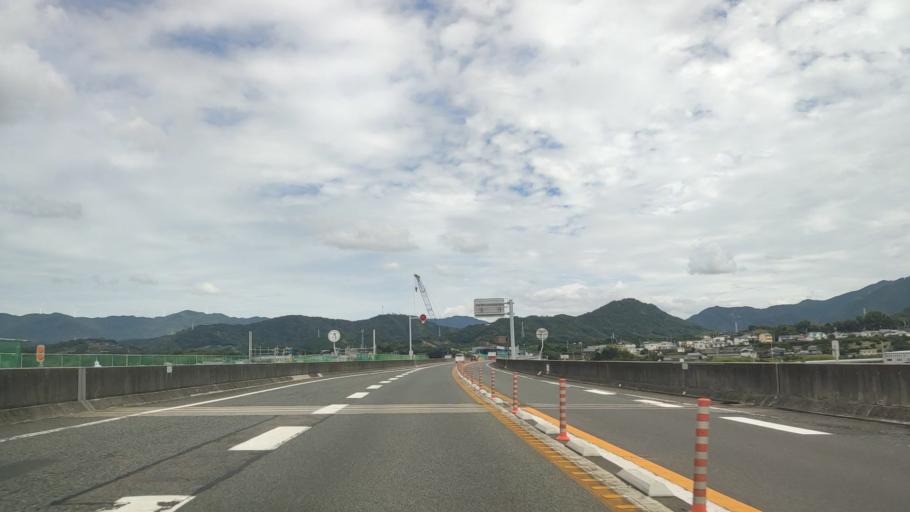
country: JP
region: Wakayama
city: Gobo
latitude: 33.9017
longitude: 135.1867
